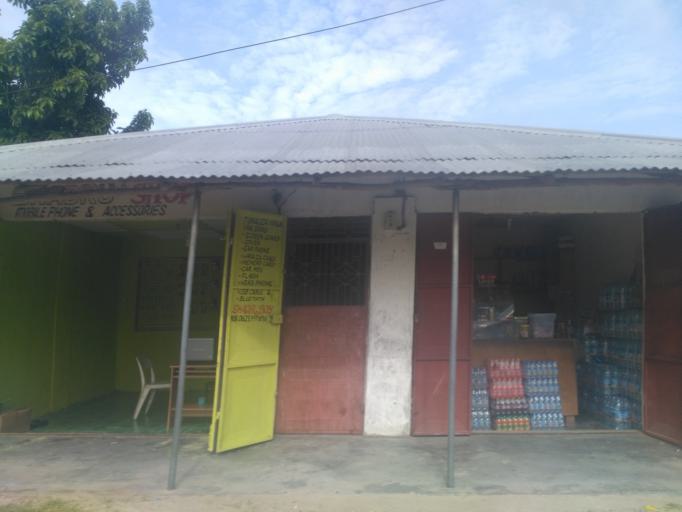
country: TZ
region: Zanzibar Urban/West
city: Zanzibar
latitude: -6.1680
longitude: 39.2098
